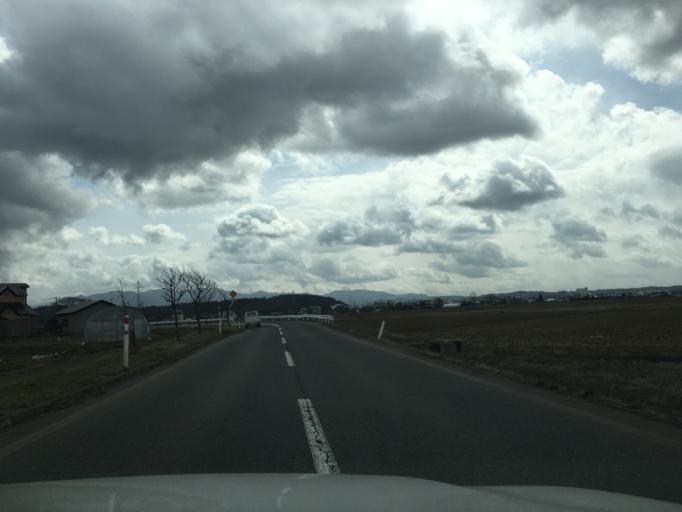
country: JP
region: Akita
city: Tenno
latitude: 39.9355
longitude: 140.0925
